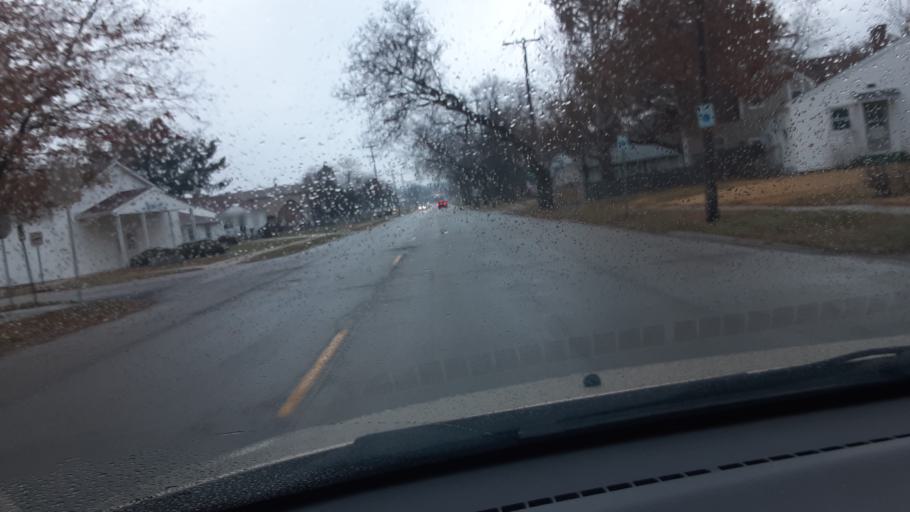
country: US
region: Illinois
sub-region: Winnebago County
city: Rockford
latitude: 42.2946
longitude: -89.1057
